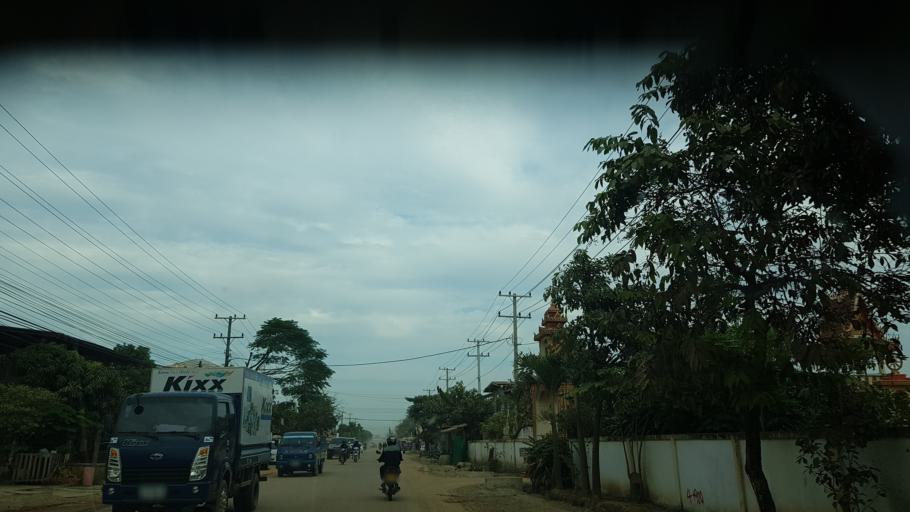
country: TH
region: Nong Khai
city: Nong Khai
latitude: 17.8863
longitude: 102.7226
